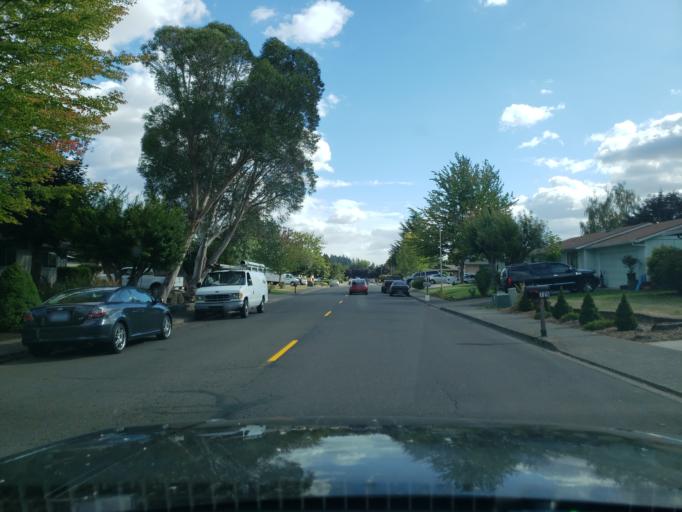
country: US
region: Oregon
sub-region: Yamhill County
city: McMinnville
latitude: 45.2041
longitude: -123.2196
